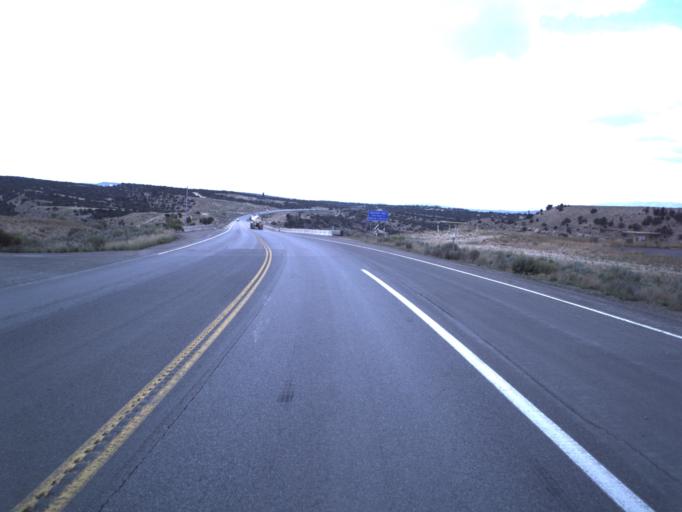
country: US
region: Utah
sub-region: Duchesne County
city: Duchesne
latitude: 40.1727
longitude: -110.4914
